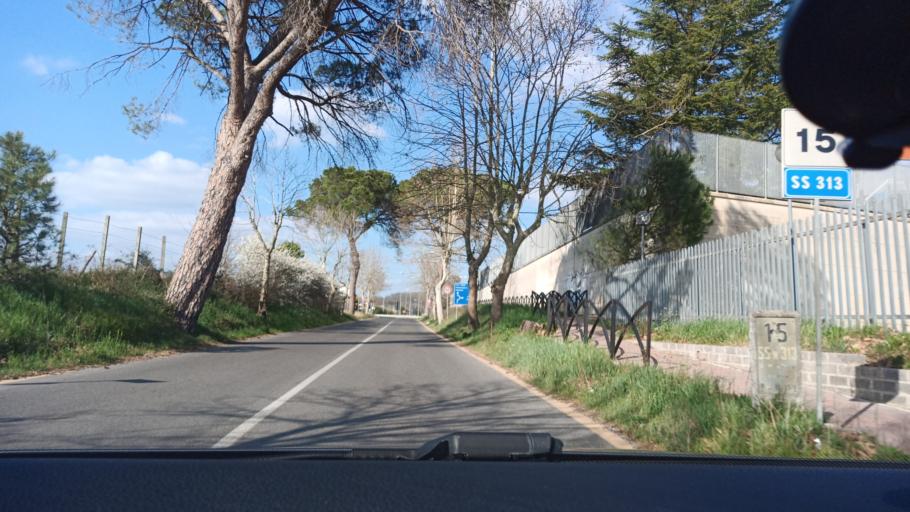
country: IT
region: Latium
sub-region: Citta metropolitana di Roma Capitale
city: Torrita Tiberina
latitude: 42.2534
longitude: 12.6376
